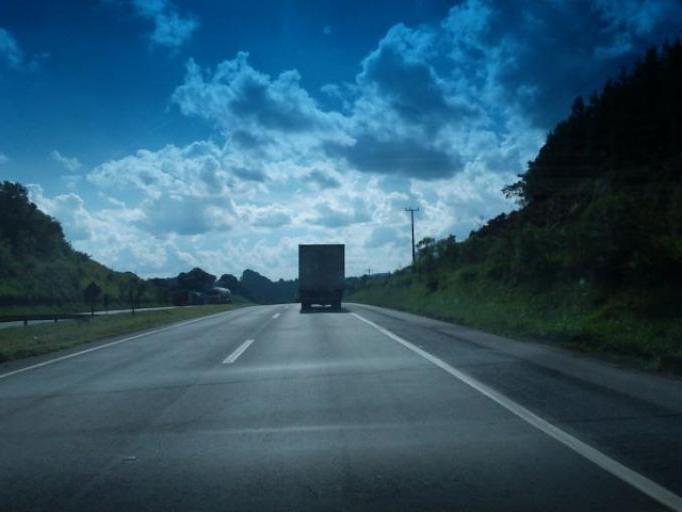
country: BR
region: Parana
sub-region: Campina Grande Do Sul
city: Campina Grande do Sul
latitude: -25.1757
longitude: -48.8714
